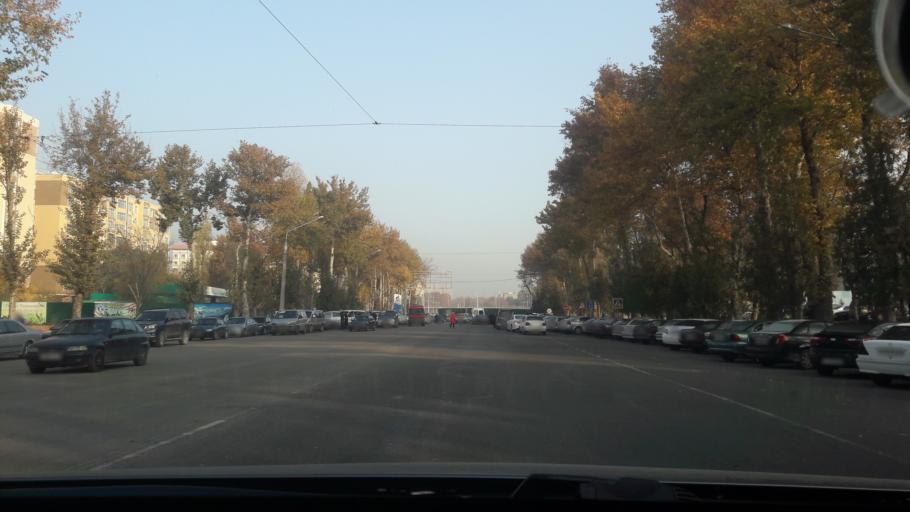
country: TJ
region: Dushanbe
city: Dushanbe
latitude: 38.5796
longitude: 68.7551
